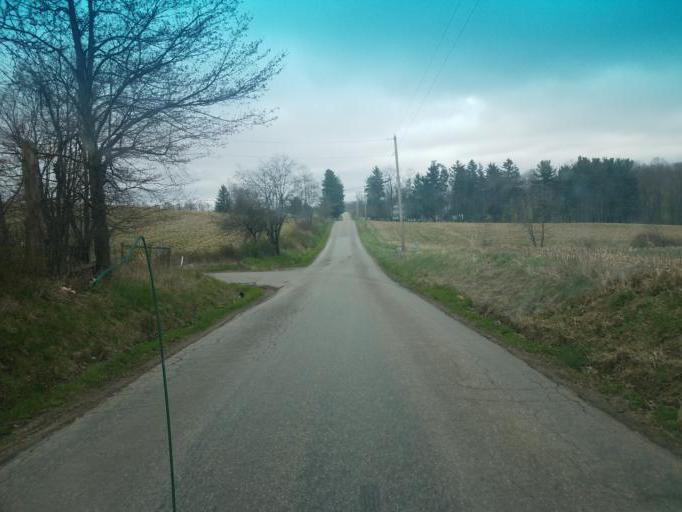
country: US
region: Ohio
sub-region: Stark County
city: Beach City
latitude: 40.6199
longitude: -81.6797
